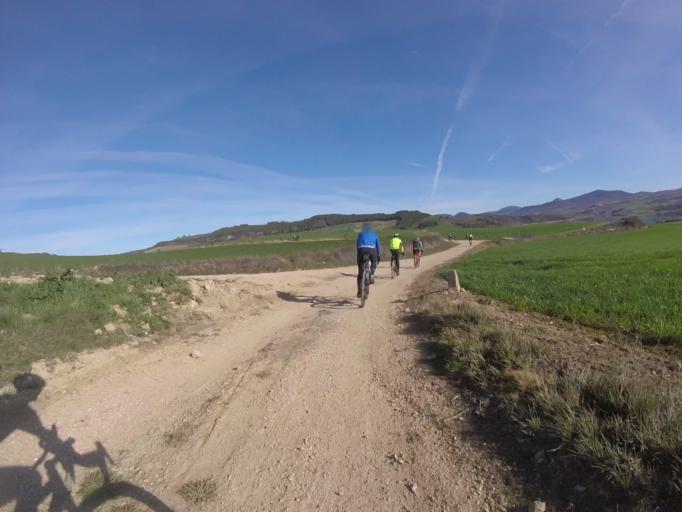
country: ES
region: Navarre
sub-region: Provincia de Navarra
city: Yerri
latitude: 42.7164
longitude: -1.9590
